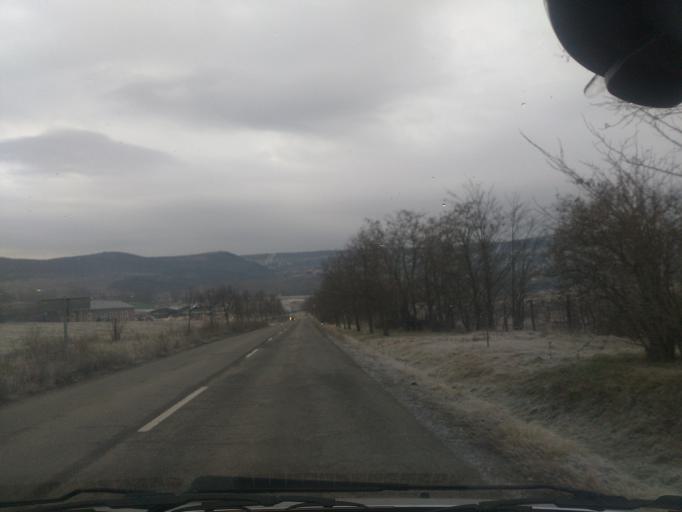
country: HU
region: Pest
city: Solymar
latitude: 47.6008
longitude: 18.9563
